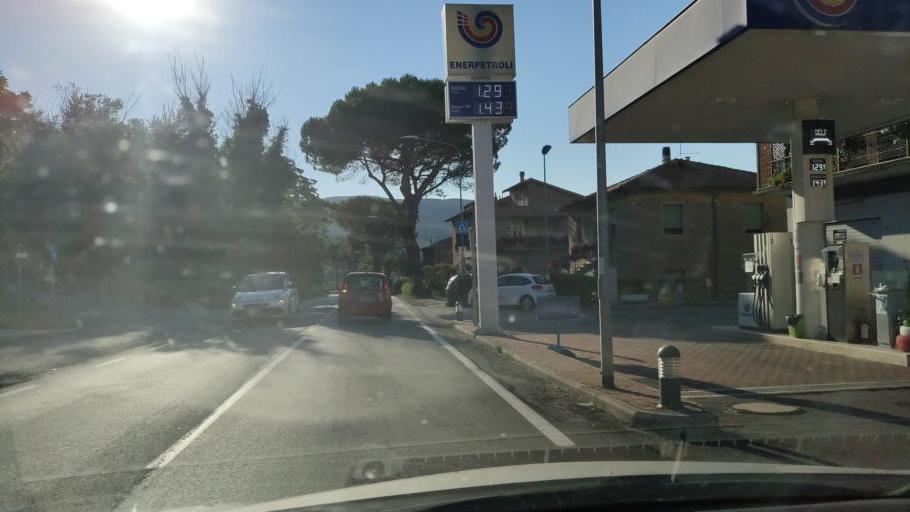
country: IT
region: Umbria
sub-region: Provincia di Terni
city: Narni
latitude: 42.5199
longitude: 12.5243
